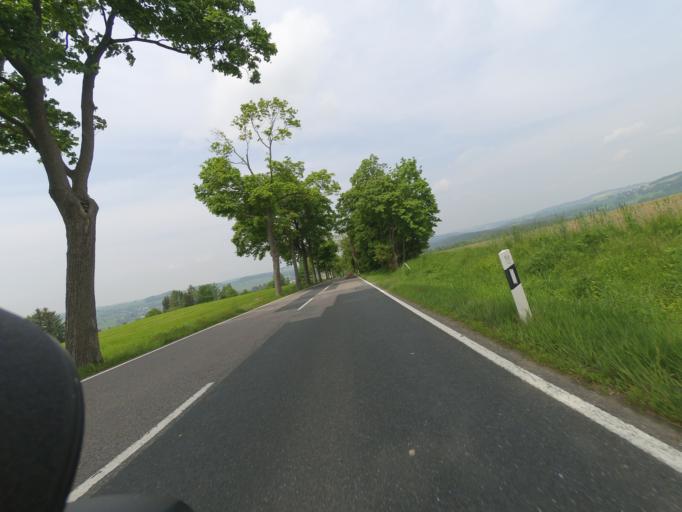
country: DE
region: Saxony
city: Wolkenstein
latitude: 50.6502
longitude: 13.0841
